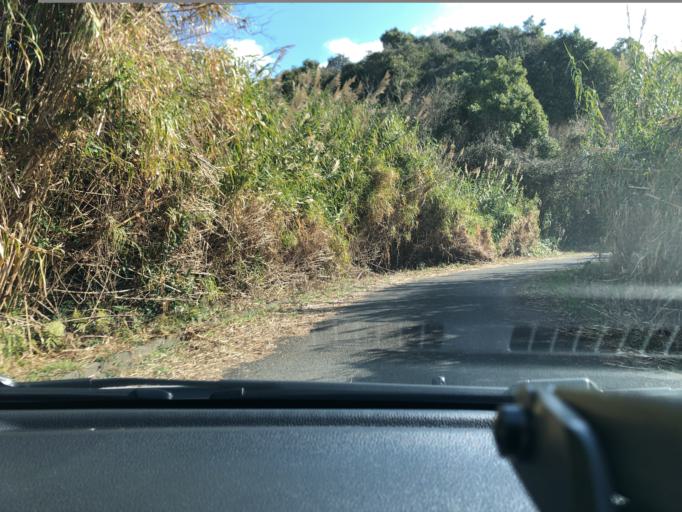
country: JP
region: Kochi
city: Sukumo
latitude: 32.9142
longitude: 132.6884
